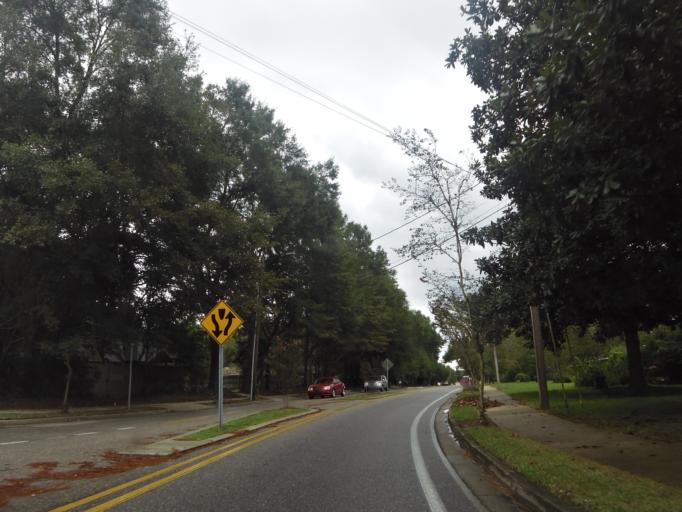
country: US
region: Alabama
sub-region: Baldwin County
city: Fairhope
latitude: 30.5236
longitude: -87.8900
